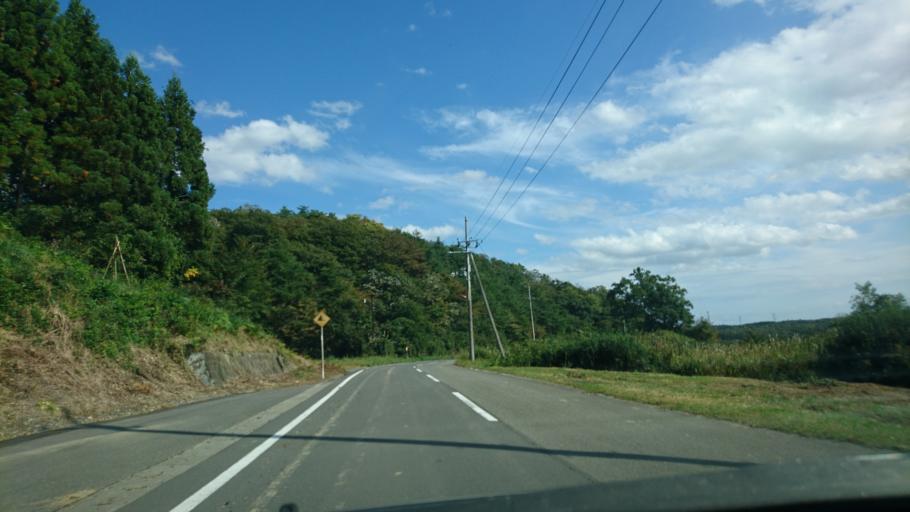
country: JP
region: Iwate
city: Ichinoseki
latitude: 38.8736
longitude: 141.0857
